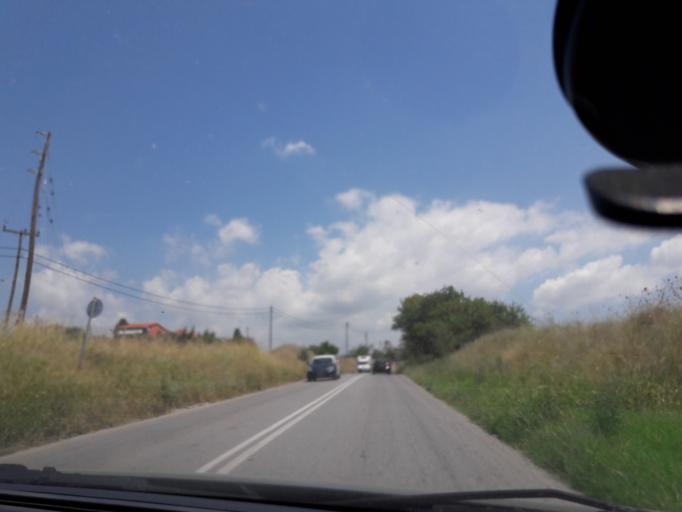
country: GR
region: Central Macedonia
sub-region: Nomos Chalkidikis
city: Nea Kallikrateia
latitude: 40.3169
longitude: 23.0701
